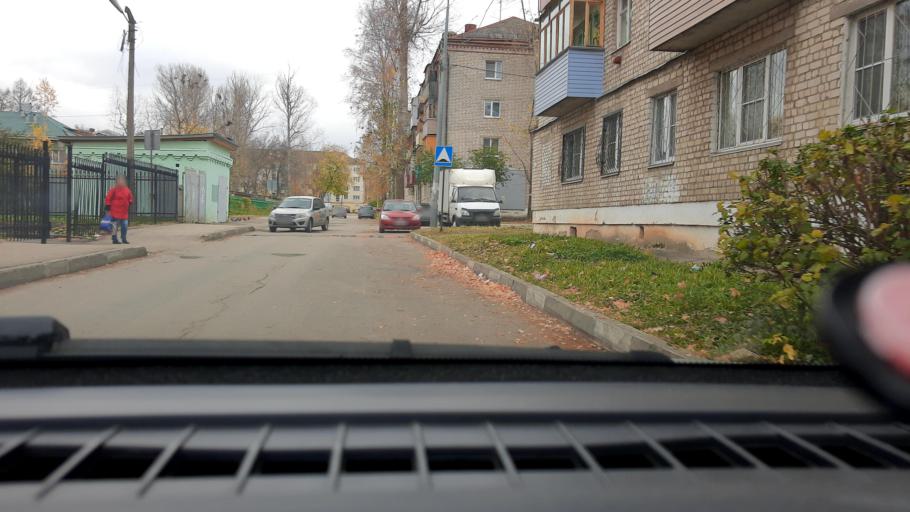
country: RU
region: Nizjnij Novgorod
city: Kstovo
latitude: 56.1493
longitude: 44.1960
